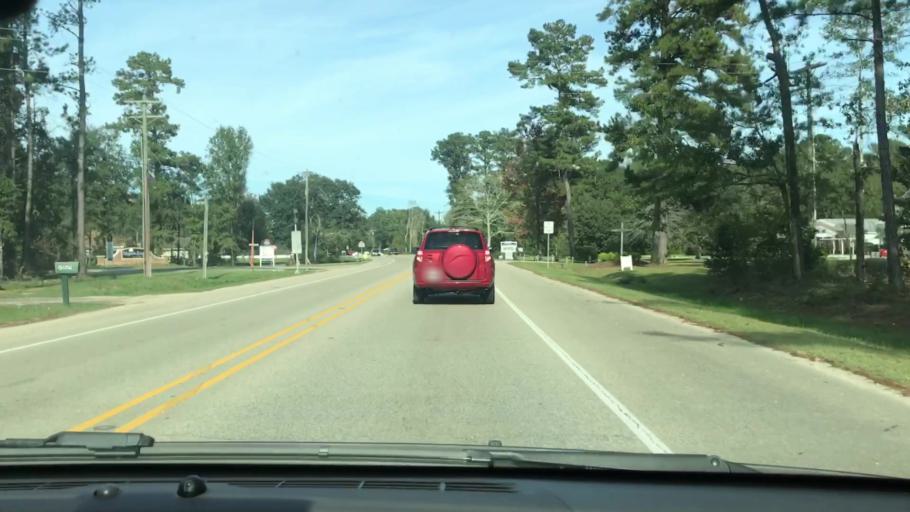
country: US
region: Louisiana
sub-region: Saint Tammany Parish
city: Pearl River
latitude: 30.3833
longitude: -89.7664
